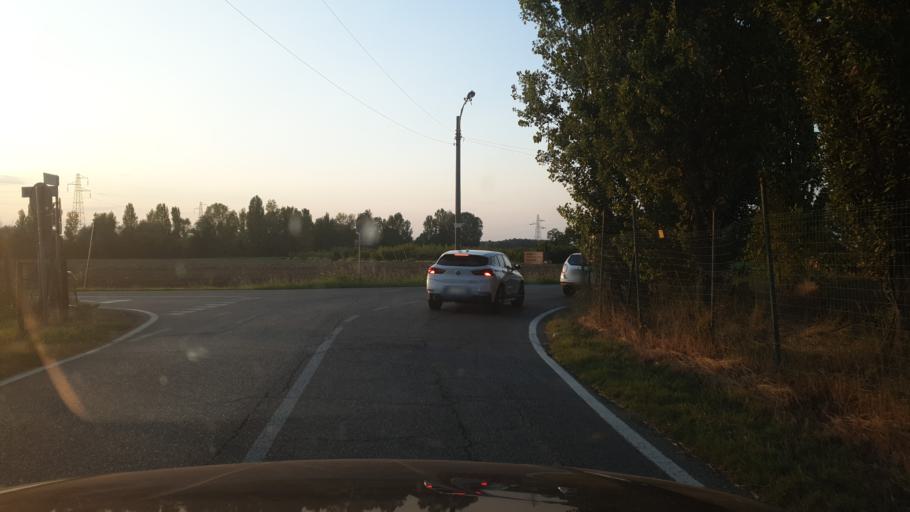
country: IT
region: Emilia-Romagna
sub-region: Provincia di Bologna
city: Quarto Inferiore
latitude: 44.5245
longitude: 11.3792
